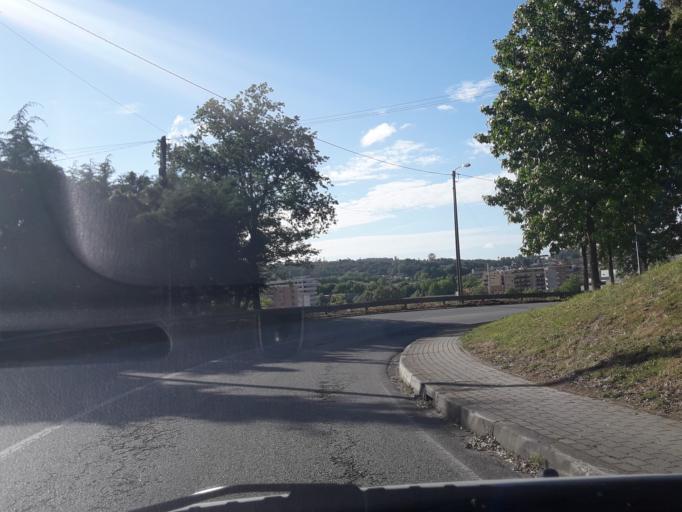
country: PT
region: Braga
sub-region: Vila Nova de Famalicao
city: Vila Nova de Famalicao
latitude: 41.3981
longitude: -8.5161
